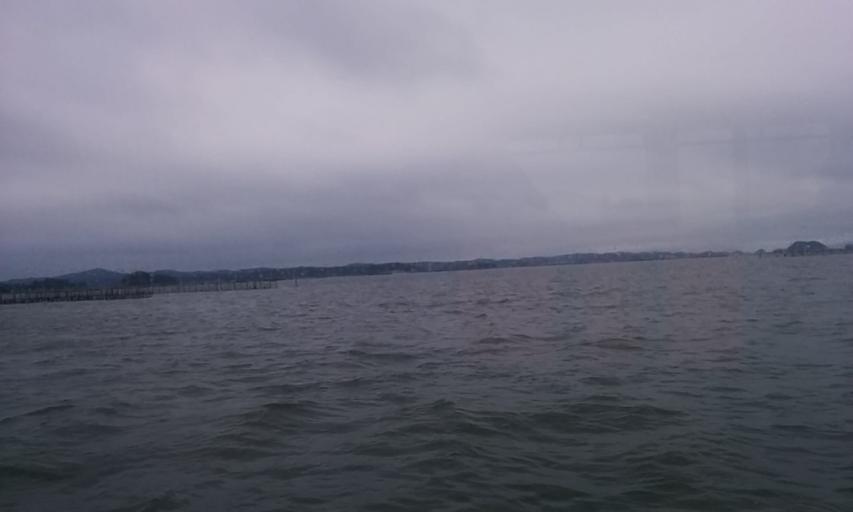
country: JP
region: Miyagi
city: Matsushima
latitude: 38.3497
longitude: 141.0796
